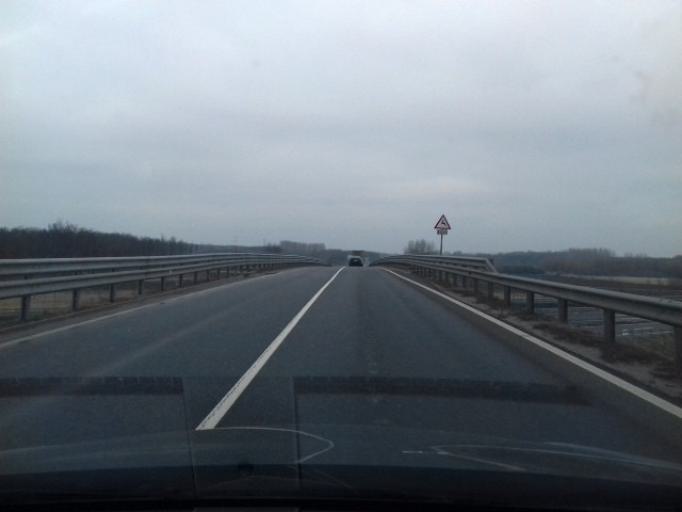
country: HU
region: Szabolcs-Szatmar-Bereg
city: Nagykallo
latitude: 47.8971
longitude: 21.8175
